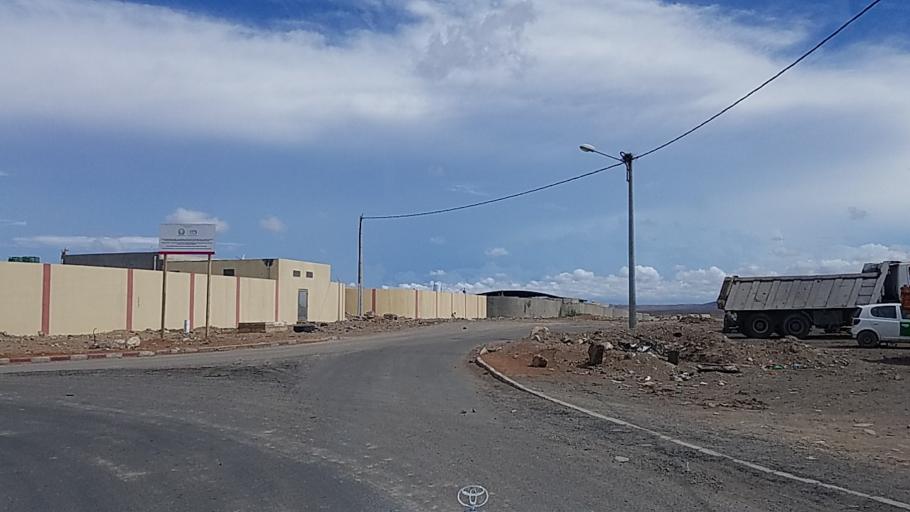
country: DJ
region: Djibouti
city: Djibouti
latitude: 11.5406
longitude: 43.1149
